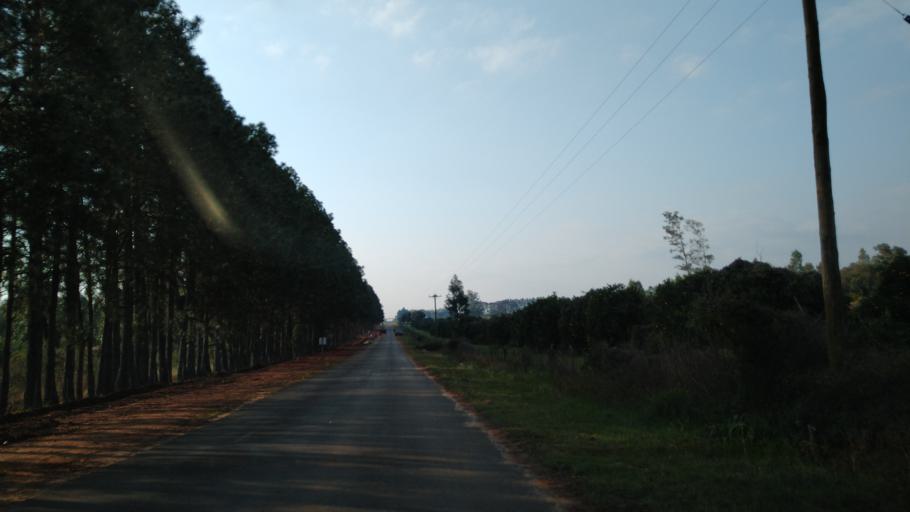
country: AR
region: Entre Rios
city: Santa Ana
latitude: -30.9086
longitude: -57.9259
